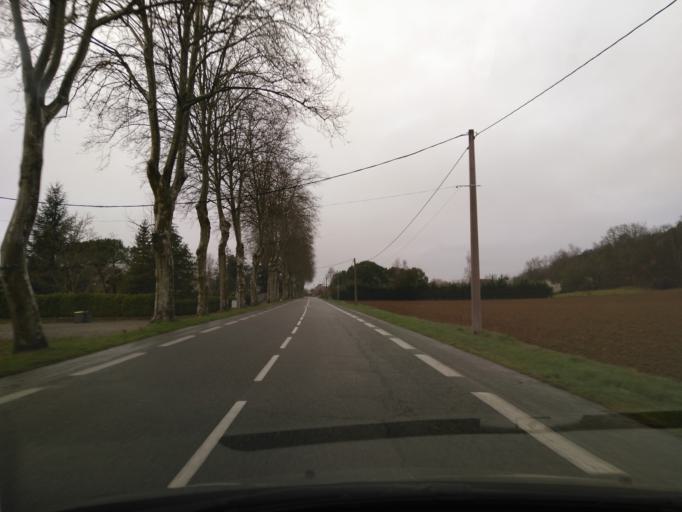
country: FR
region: Midi-Pyrenees
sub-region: Departement de la Haute-Garonne
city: Rieux-Volvestre
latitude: 43.2493
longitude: 1.2021
